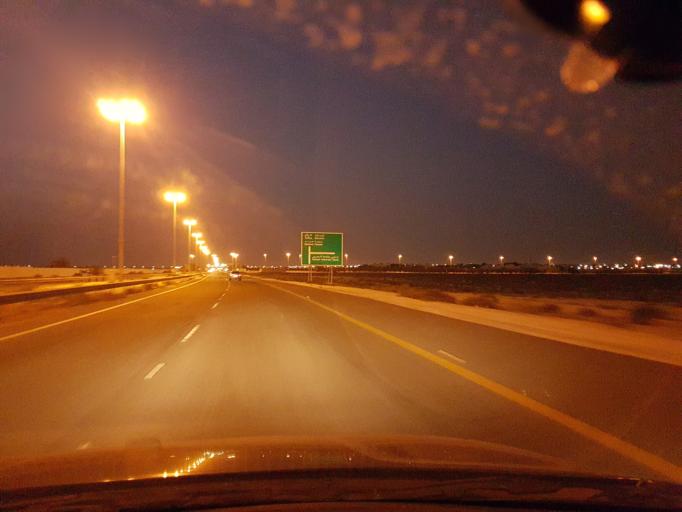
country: BH
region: Central Governorate
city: Dar Kulayb
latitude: 26.0336
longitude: 50.5000
